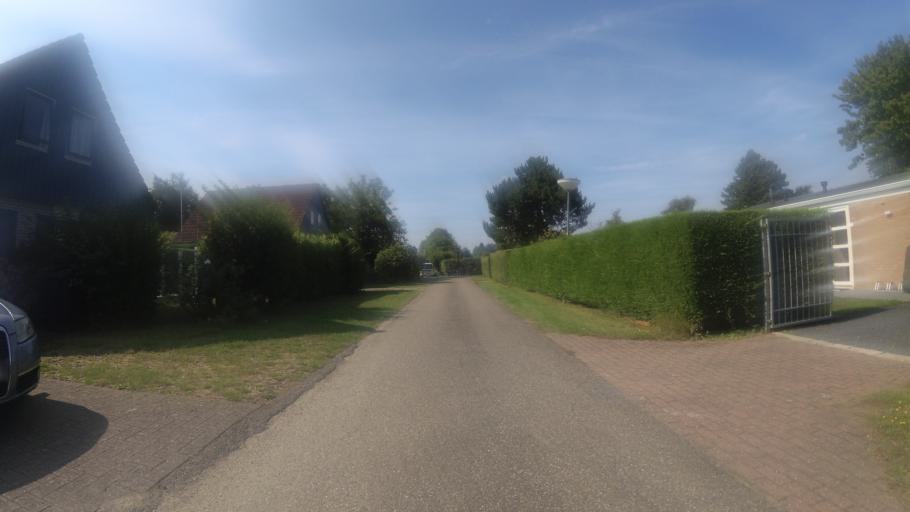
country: NL
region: Zeeland
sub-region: Gemeente Noord-Beveland
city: Kamperland
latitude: 51.5611
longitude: 3.6921
